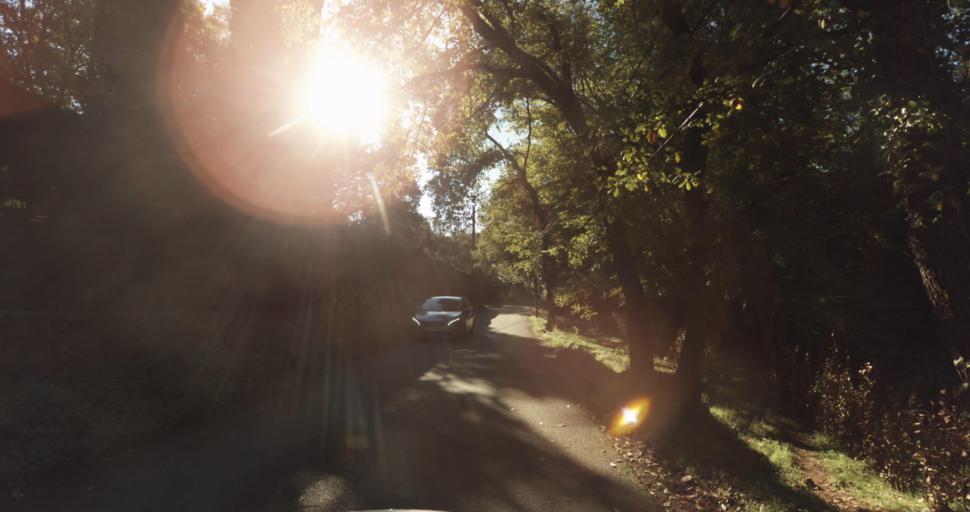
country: FR
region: Provence-Alpes-Cote d'Azur
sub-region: Departement des Alpes-Maritimes
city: Vence
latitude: 43.7111
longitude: 7.1052
